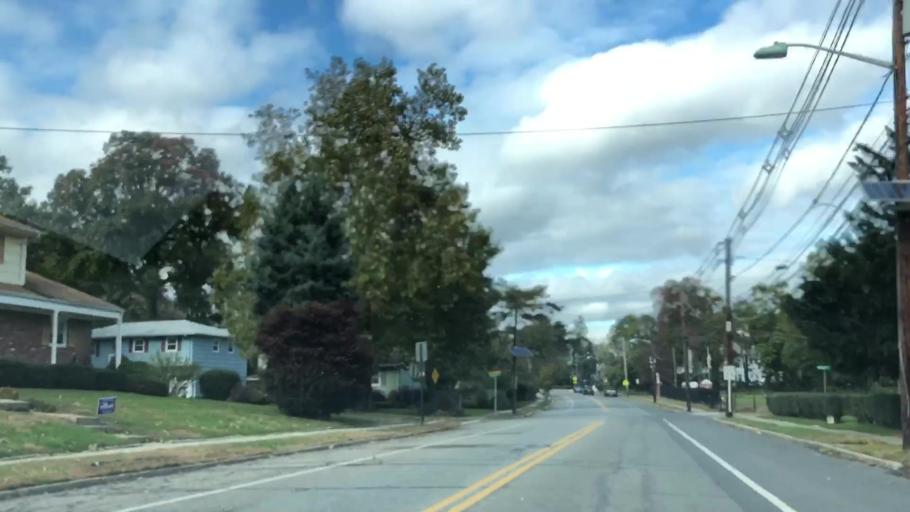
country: US
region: New Jersey
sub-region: Essex County
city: Glen Ridge
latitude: 40.7999
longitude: -74.2189
